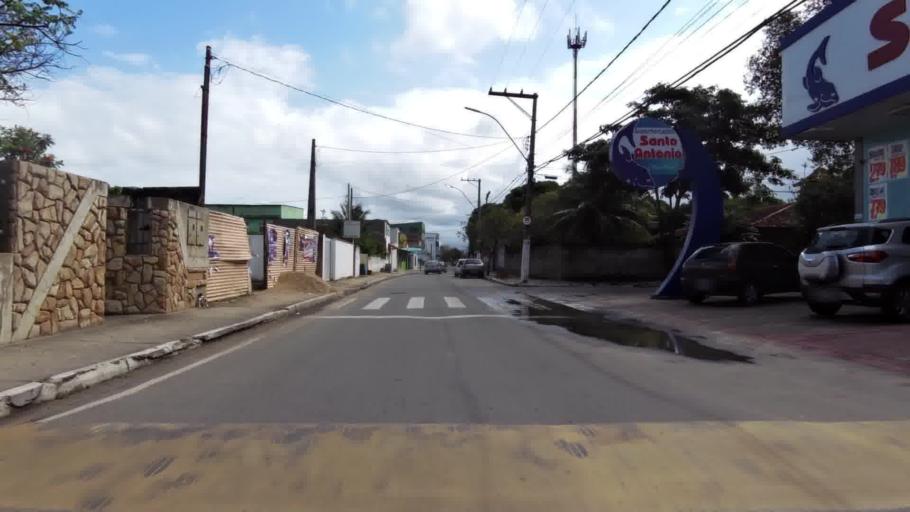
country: BR
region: Espirito Santo
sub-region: Piuma
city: Piuma
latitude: -20.8082
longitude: -40.6435
